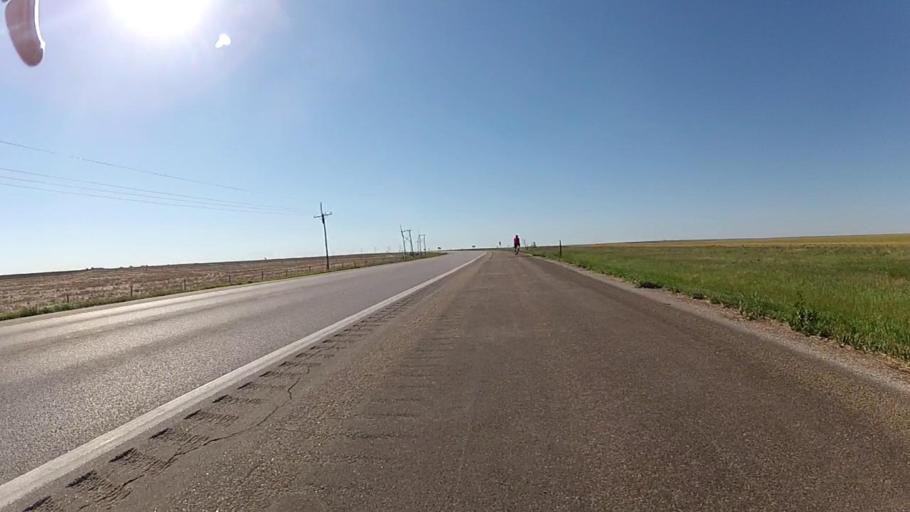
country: US
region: Kansas
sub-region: Ford County
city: Dodge City
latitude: 37.5895
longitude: -99.6872
